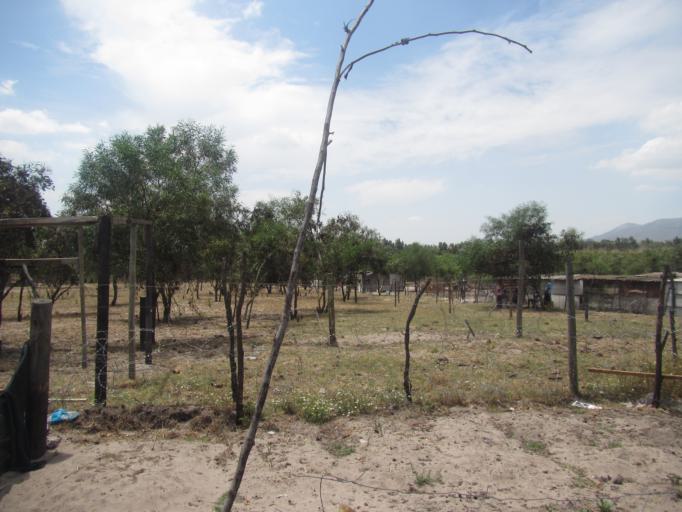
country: ZA
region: Western Cape
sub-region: Cape Winelands District Municipality
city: Stellenbosch
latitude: -33.8043
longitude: 18.8564
